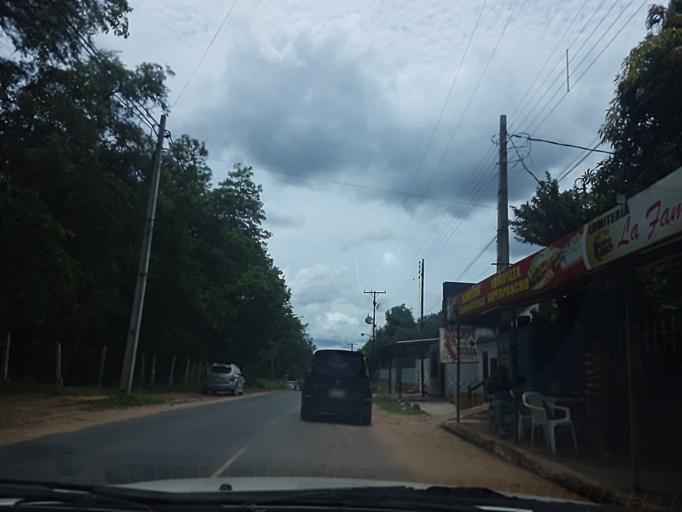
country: PY
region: Central
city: Colonia Mariano Roque Alonso
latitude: -25.1870
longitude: -57.5413
